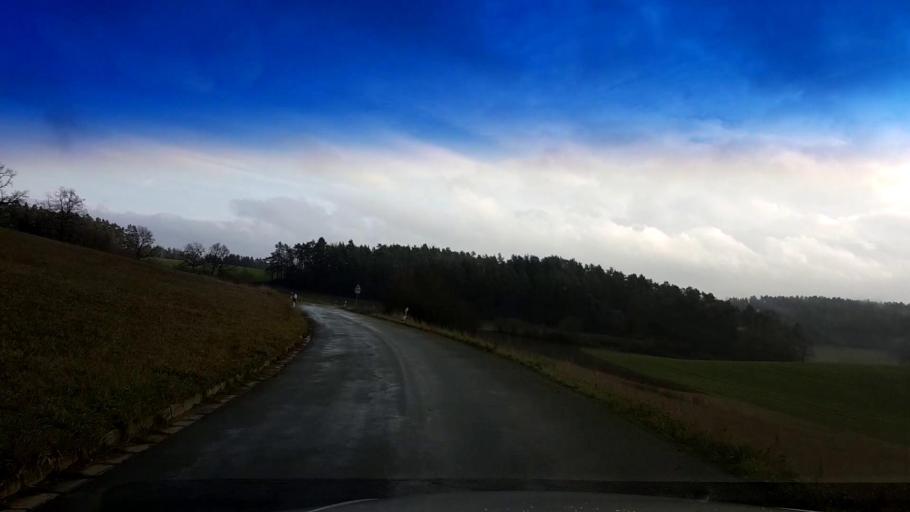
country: DE
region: Bavaria
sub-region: Upper Franconia
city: Poxdorf
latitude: 49.9319
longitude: 11.1260
